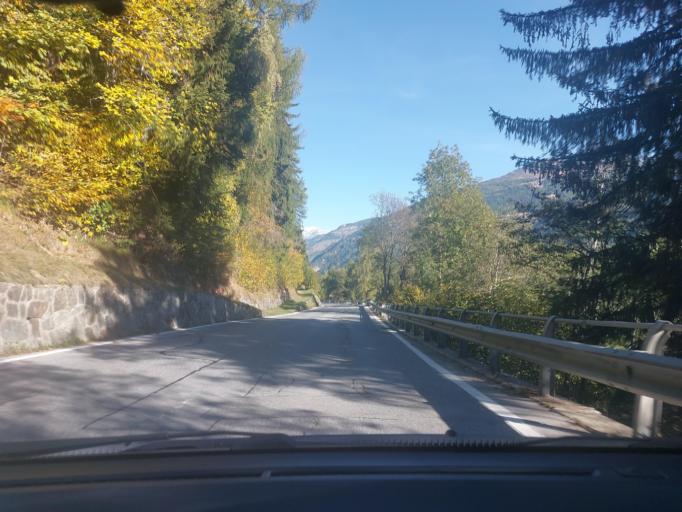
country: CH
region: Valais
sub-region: Sierre District
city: Chippis
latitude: 46.1900
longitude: 7.5844
